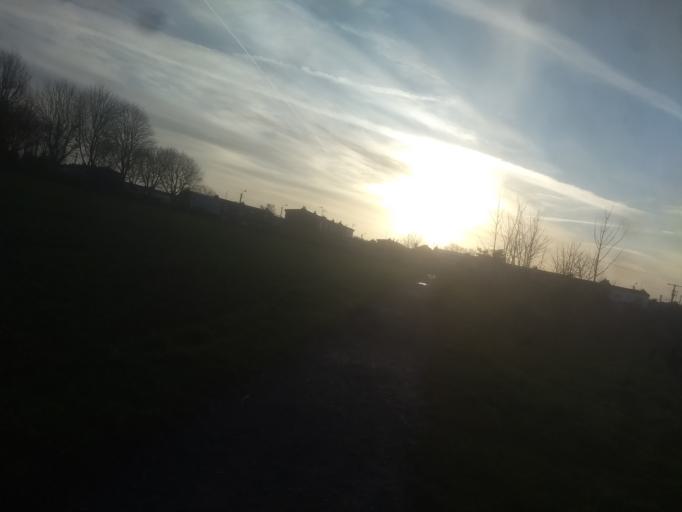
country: FR
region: Nord-Pas-de-Calais
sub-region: Departement du Pas-de-Calais
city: Beaurains
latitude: 50.2737
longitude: 2.7912
